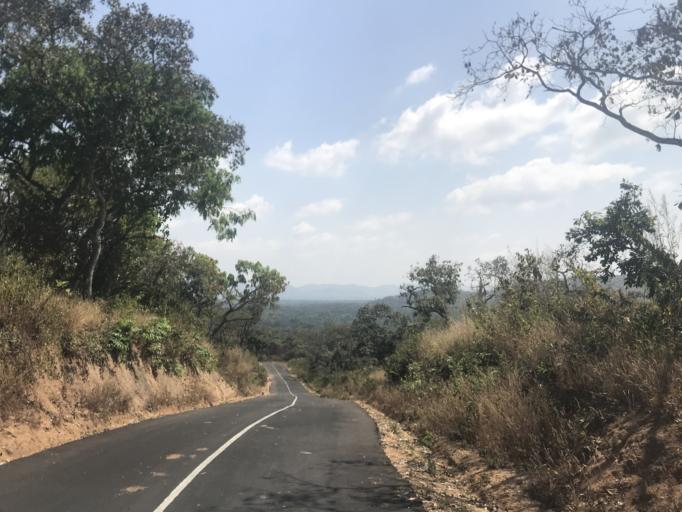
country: NG
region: Osun
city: Otan Ayegbaju
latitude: 7.8953
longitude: 4.8421
